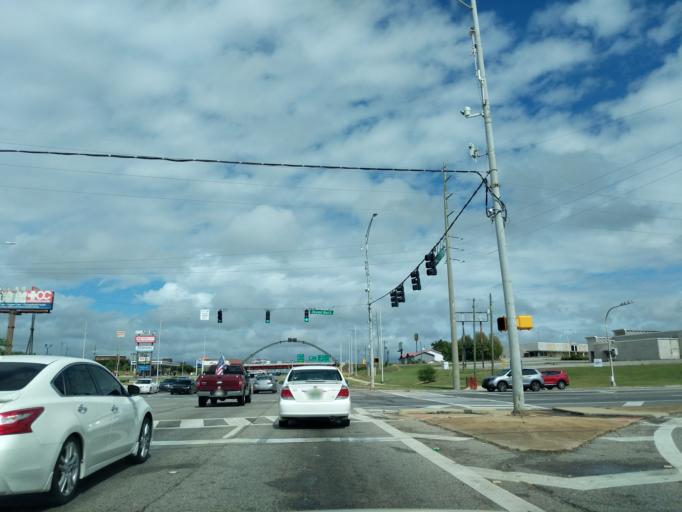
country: US
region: Alabama
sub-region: Tuscaloosa County
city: Tuscaloosa
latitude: 33.1677
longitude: -87.5253
